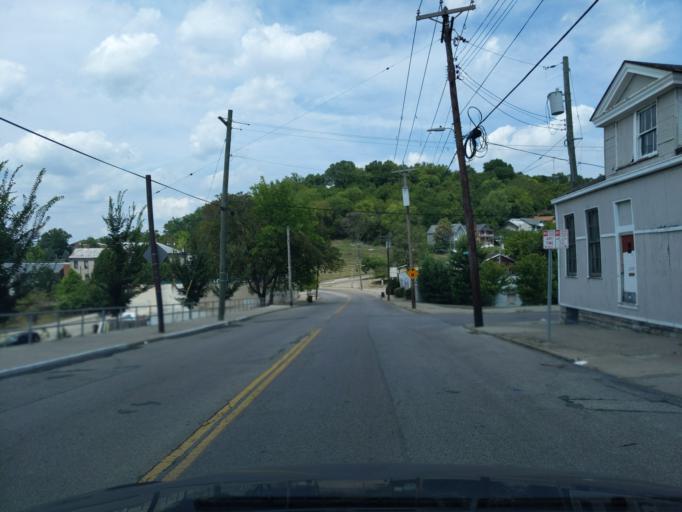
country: US
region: Kentucky
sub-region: Kenton County
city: Ludlow
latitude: 39.1308
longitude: -84.5305
